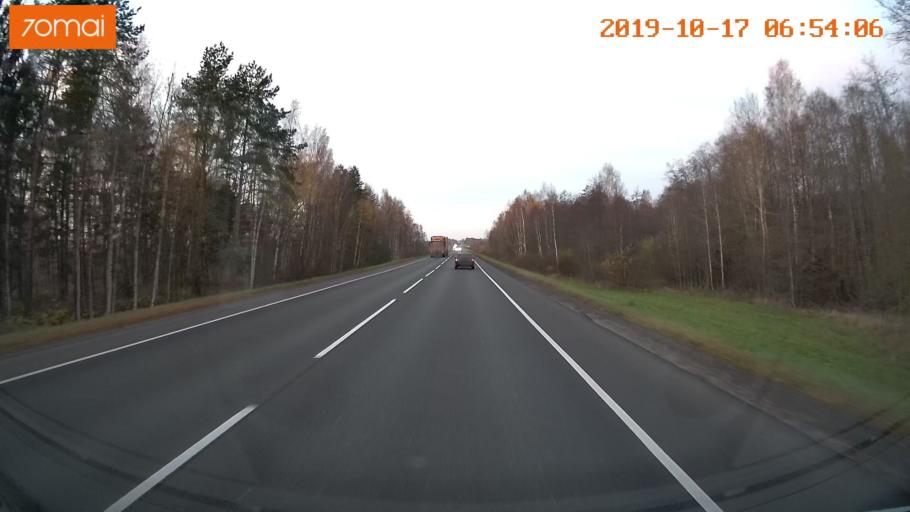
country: RU
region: Vladimir
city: Suzdal'
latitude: 56.4676
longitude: 40.4756
